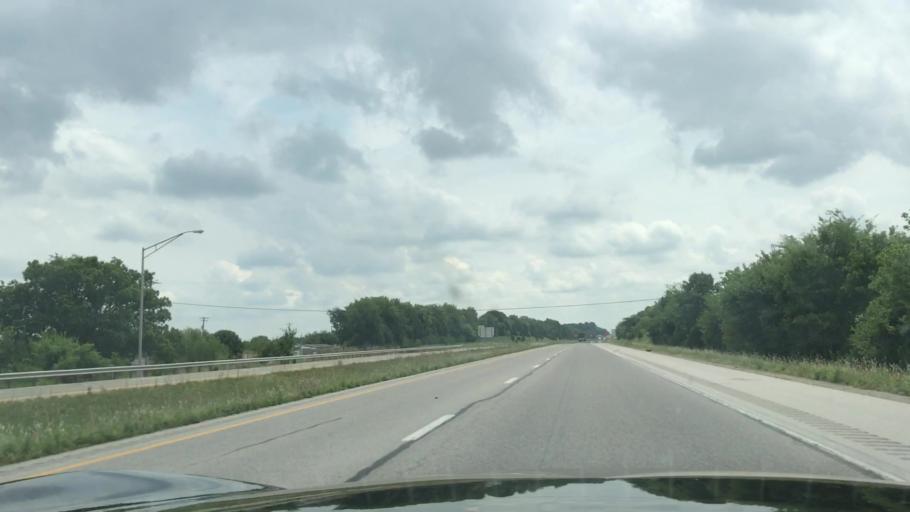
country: US
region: Kentucky
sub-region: Warren County
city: Bowling Green
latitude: 36.9892
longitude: -86.5034
